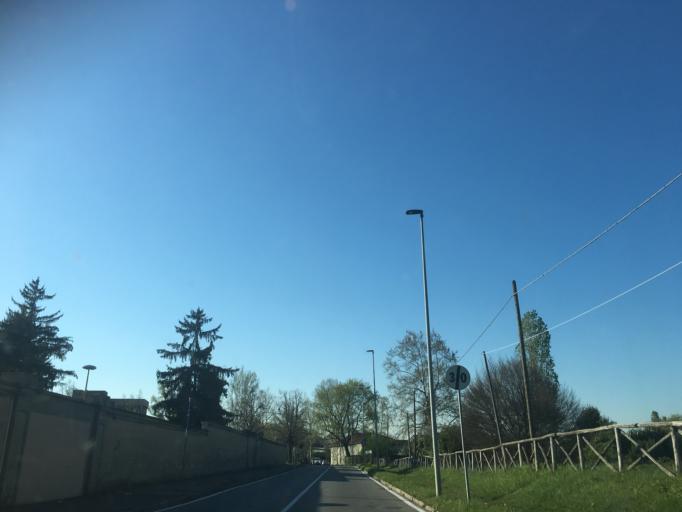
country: IT
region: Piedmont
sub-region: Provincia di Torino
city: Turin
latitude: 45.0844
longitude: 7.7139
